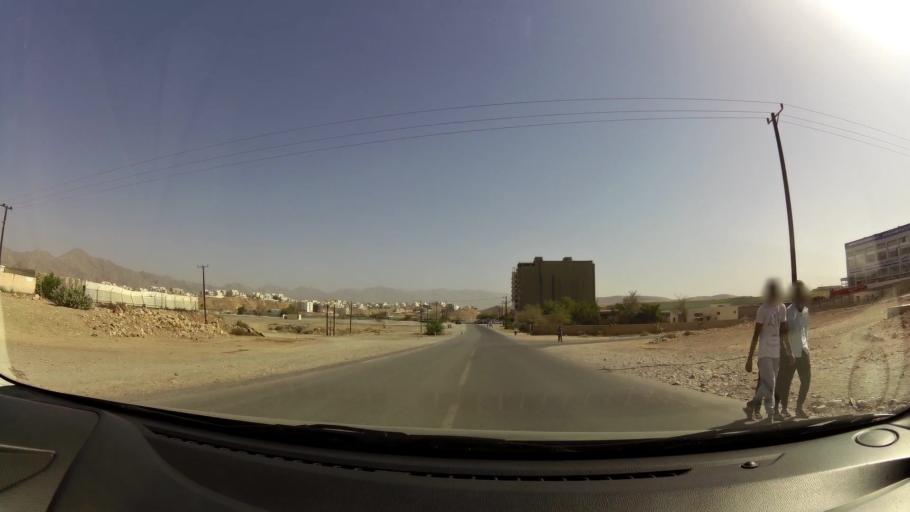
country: OM
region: Muhafazat Masqat
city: Bawshar
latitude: 23.5675
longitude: 58.3483
